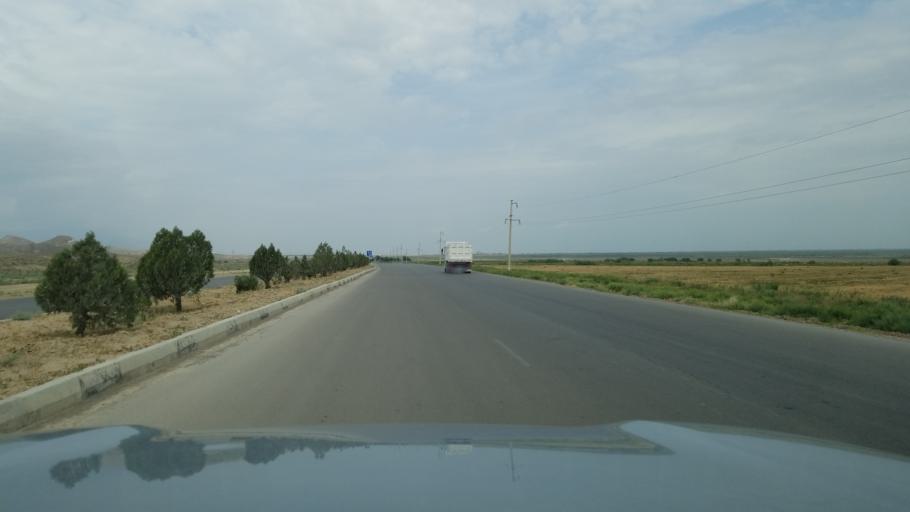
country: TM
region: Ahal
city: Baharly
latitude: 38.2405
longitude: 57.7677
